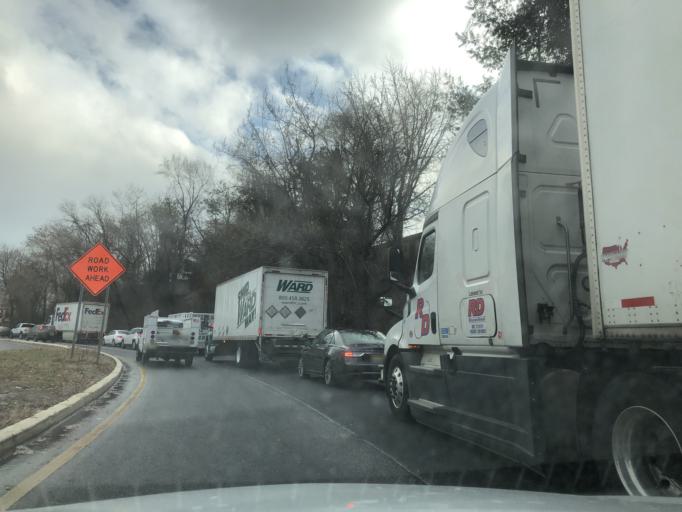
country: US
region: New Jersey
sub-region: Camden County
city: Mount Ephraim
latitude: 39.8717
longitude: -75.0836
